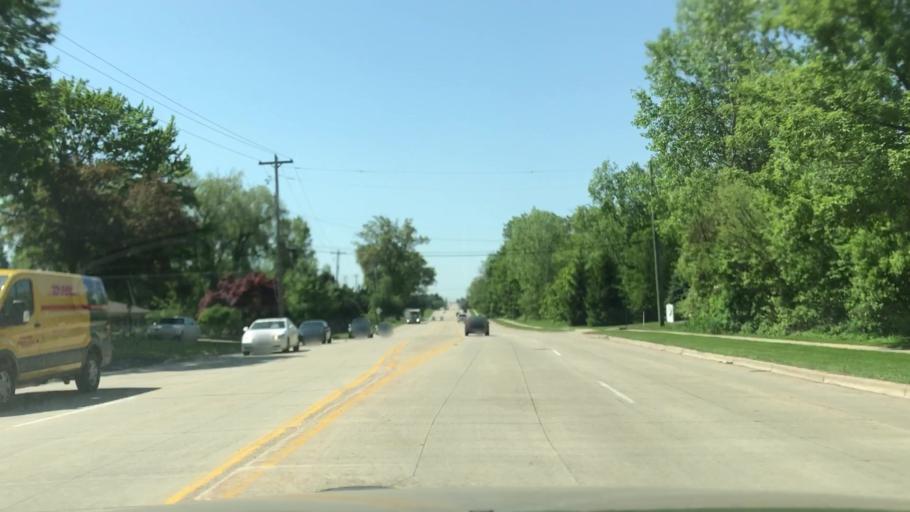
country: US
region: Michigan
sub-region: Kent County
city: East Grand Rapids
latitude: 42.9191
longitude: -85.5494
